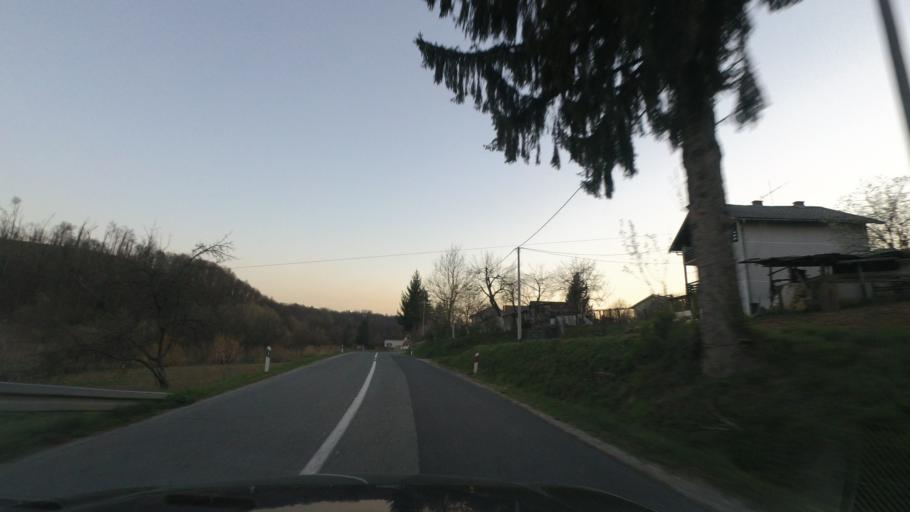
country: HR
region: Karlovacka
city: Vojnic
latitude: 45.3311
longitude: 15.7137
